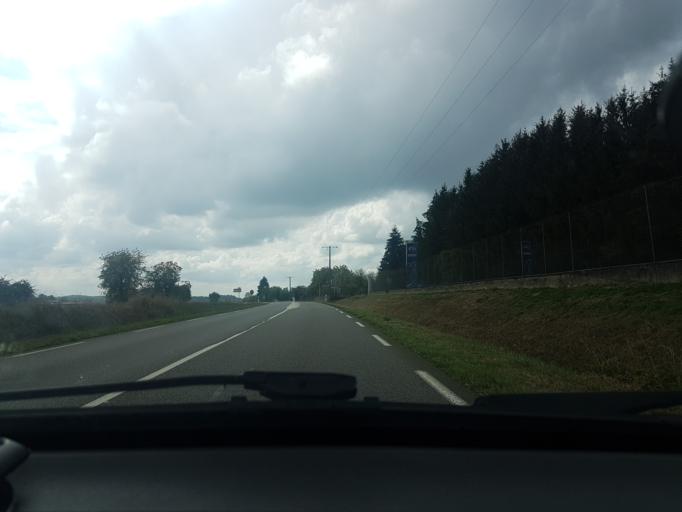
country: FR
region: Franche-Comte
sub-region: Departement de la Haute-Saone
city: Villersexel
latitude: 47.5484
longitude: 6.4402
